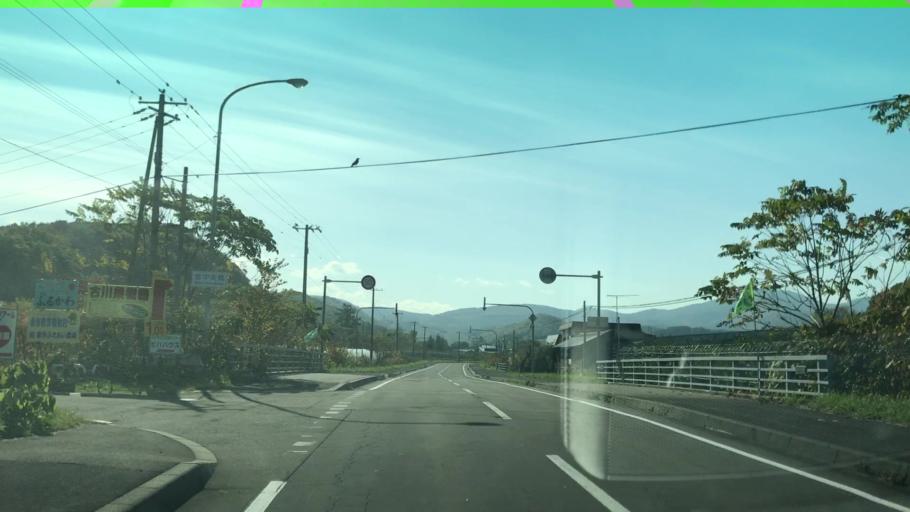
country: JP
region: Hokkaido
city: Yoichi
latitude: 43.1730
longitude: 140.8217
